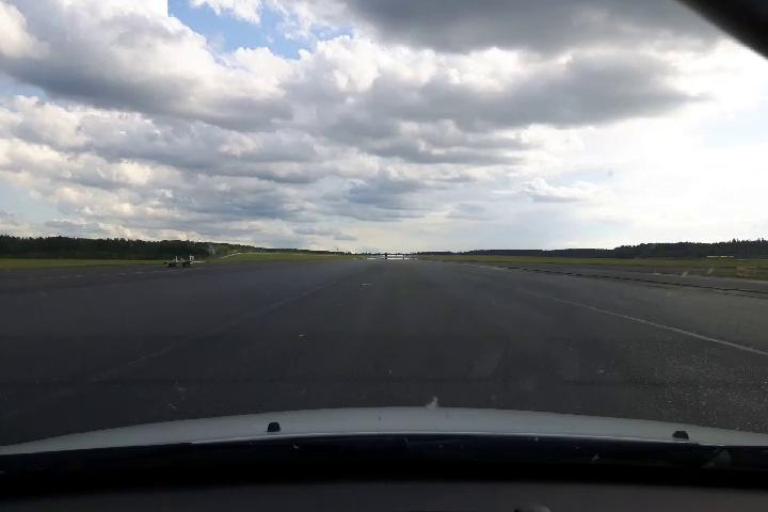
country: SE
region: Stockholm
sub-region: Sigtuna Kommun
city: Rosersberg
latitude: 59.6409
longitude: 17.9558
